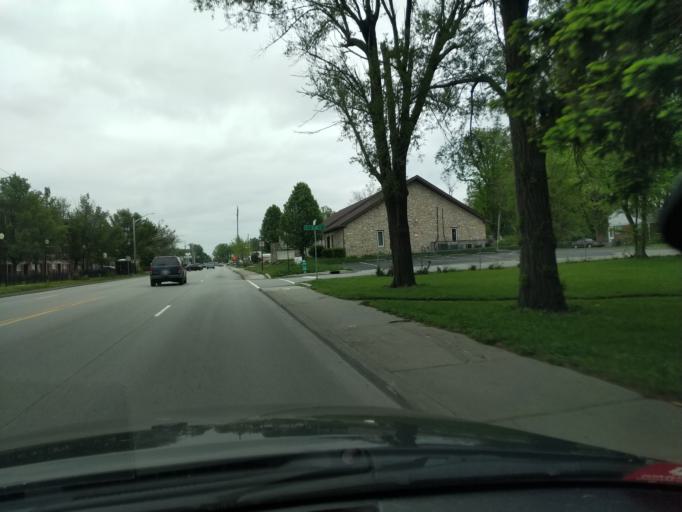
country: US
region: Indiana
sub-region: Marion County
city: Broad Ripple
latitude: 39.8253
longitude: -86.1075
